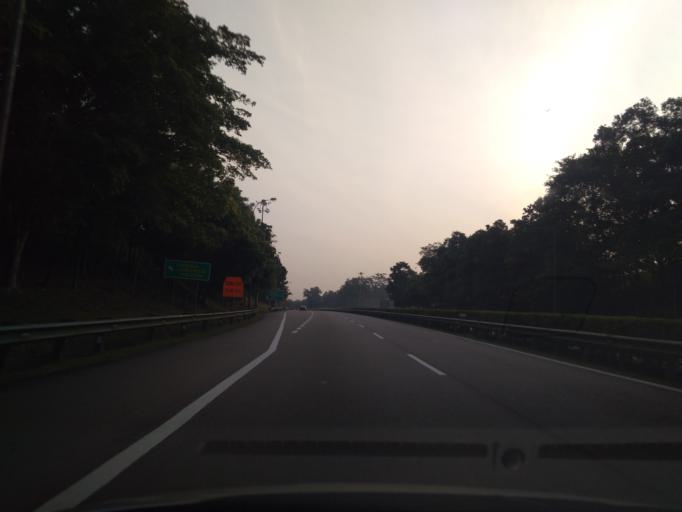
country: MY
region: Johor
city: Taman Senai
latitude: 1.5895
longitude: 103.6108
